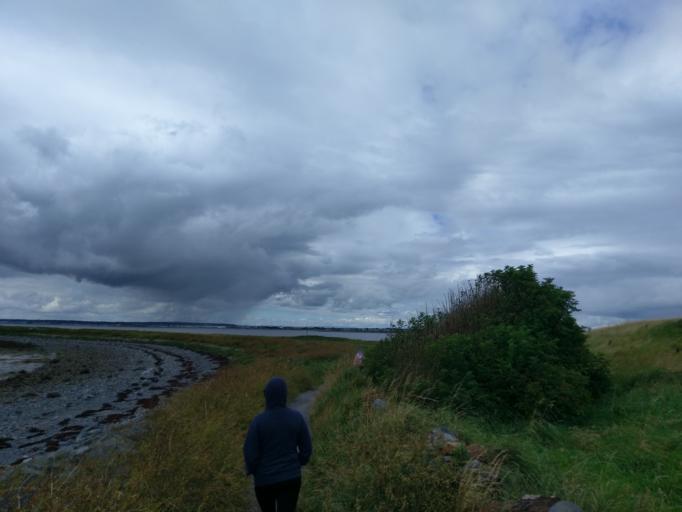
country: IE
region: Connaught
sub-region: County Galway
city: Gaillimh
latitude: 53.2465
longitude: -8.9859
